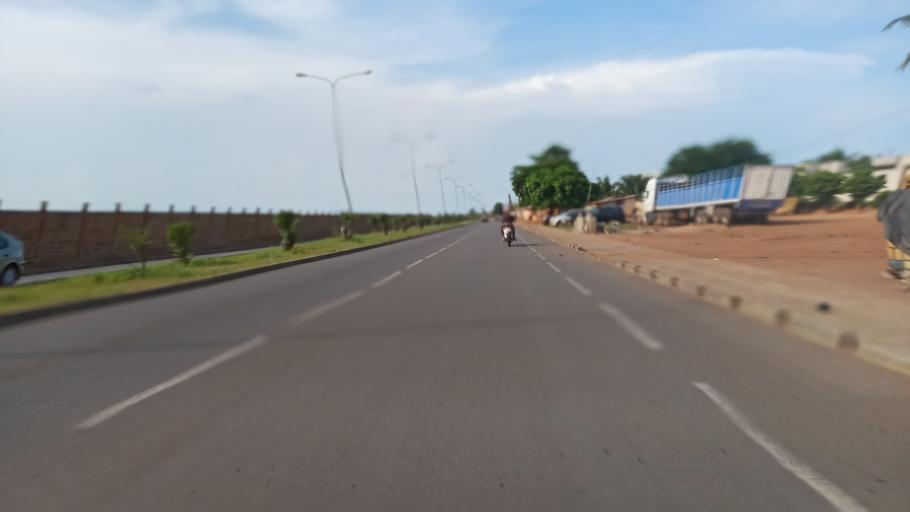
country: TG
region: Maritime
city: Lome
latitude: 6.1798
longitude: 1.2685
